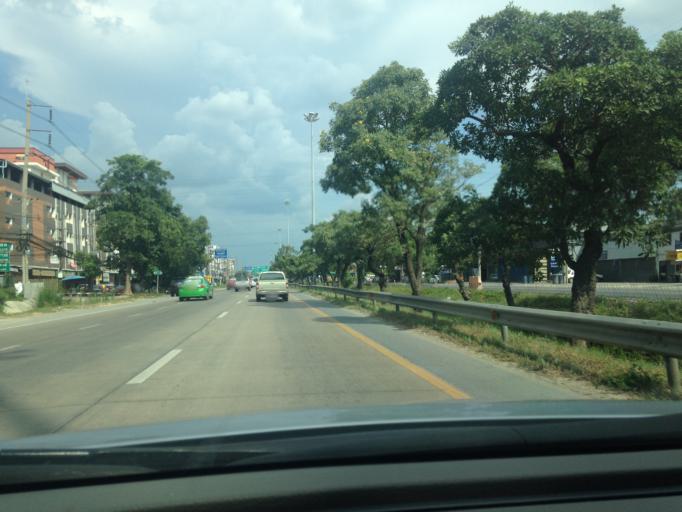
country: TH
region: Pathum Thani
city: Khlong Luang
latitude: 14.0655
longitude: 100.6039
